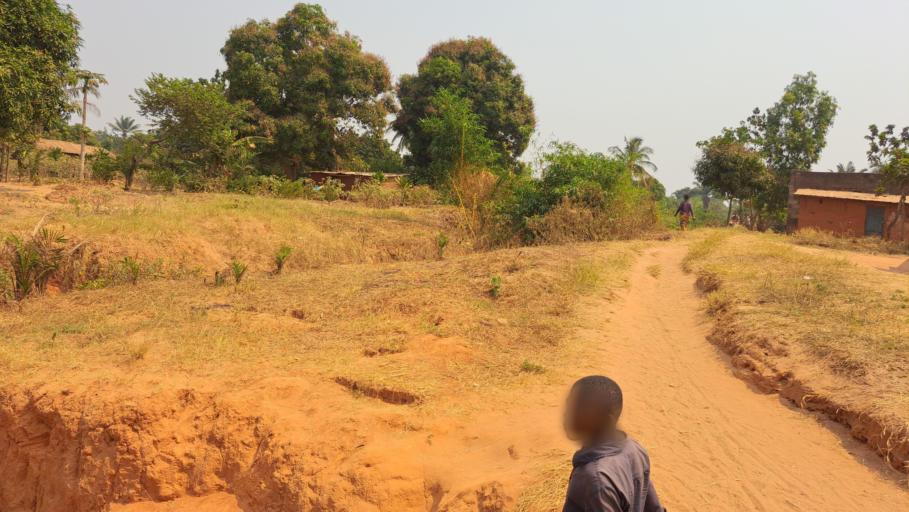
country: CD
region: Kasai-Oriental
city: Mbuji-Mayi
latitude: -6.0985
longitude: 23.5636
